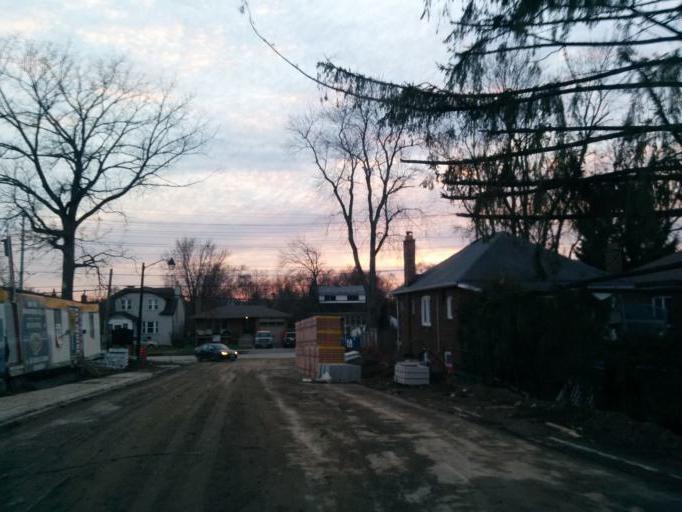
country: CA
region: Ontario
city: Etobicoke
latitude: 43.5834
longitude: -79.5592
